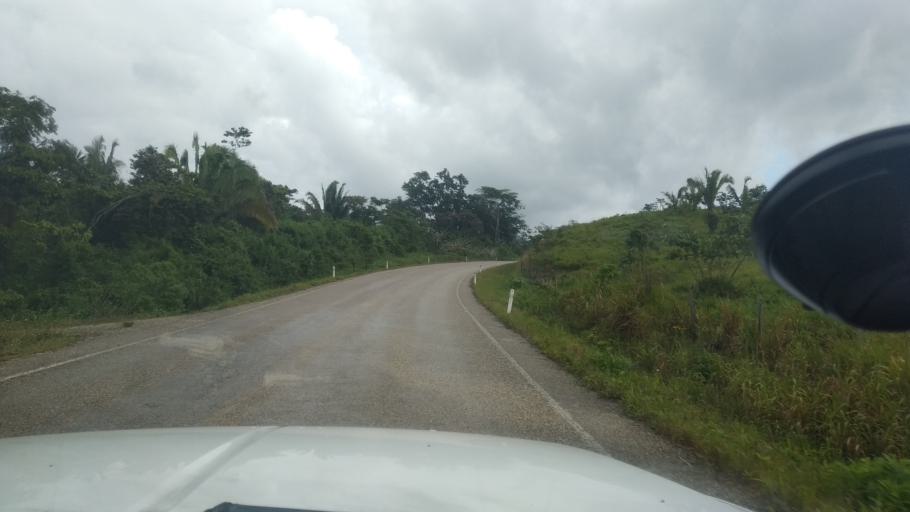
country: GT
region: Peten
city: San Luis
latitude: 16.1990
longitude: -89.1534
